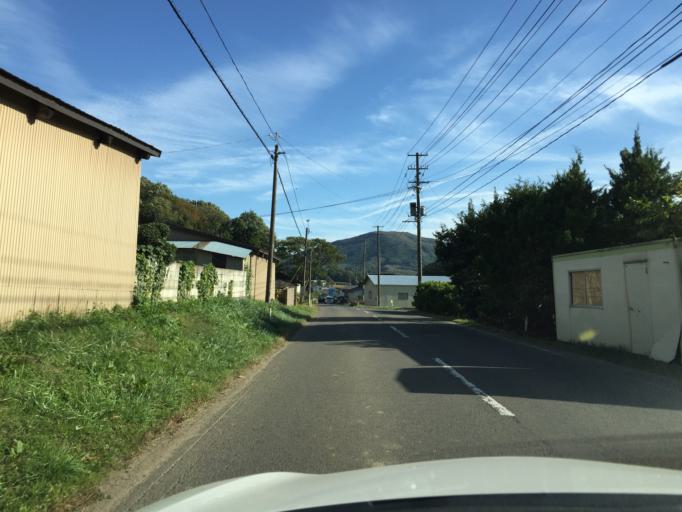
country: JP
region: Fukushima
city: Funehikimachi-funehiki
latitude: 37.3503
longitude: 140.5524
